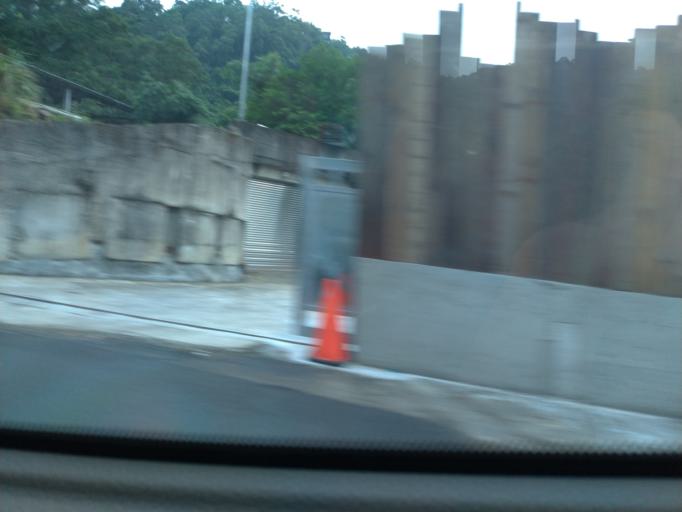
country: TW
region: Taipei
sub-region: Taipei
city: Banqiao
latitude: 24.9236
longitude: 121.4264
